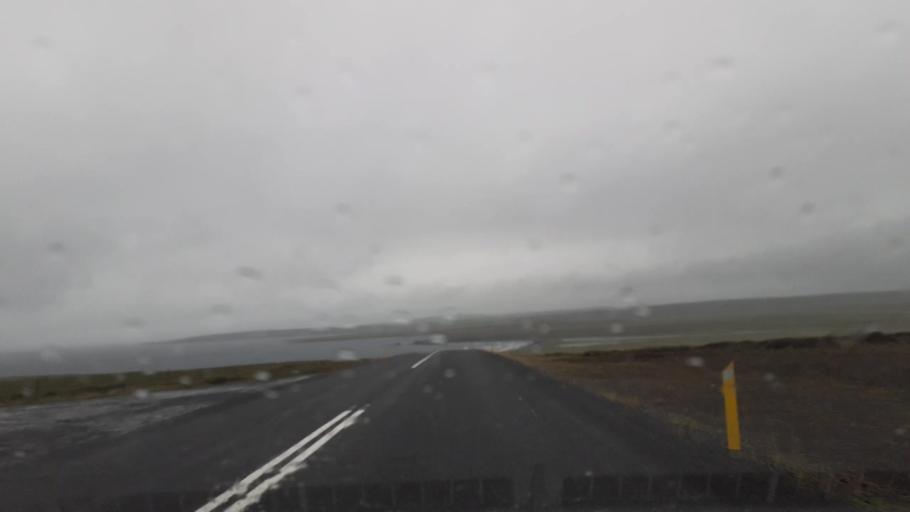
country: IS
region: Northeast
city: Husavik
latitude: 66.2309
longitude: -15.7233
